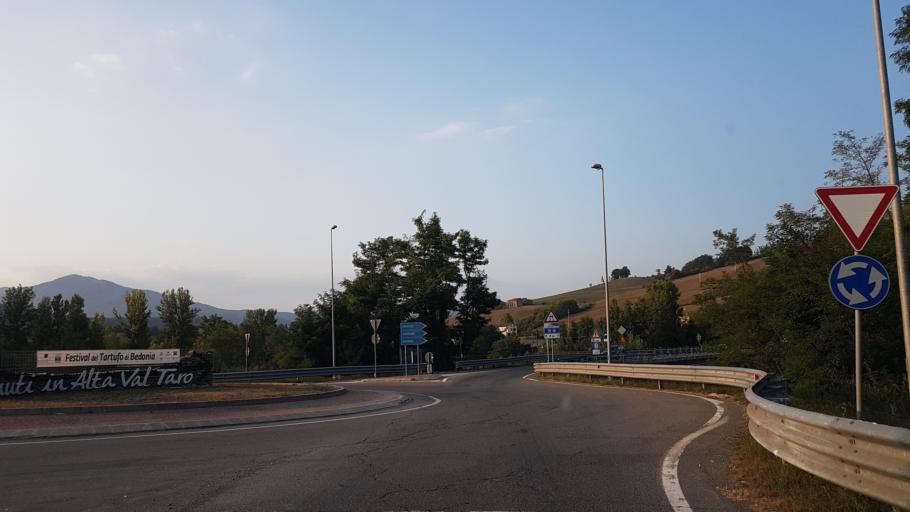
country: IT
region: Emilia-Romagna
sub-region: Provincia di Parma
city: Albareto
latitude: 44.4776
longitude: 9.7114
